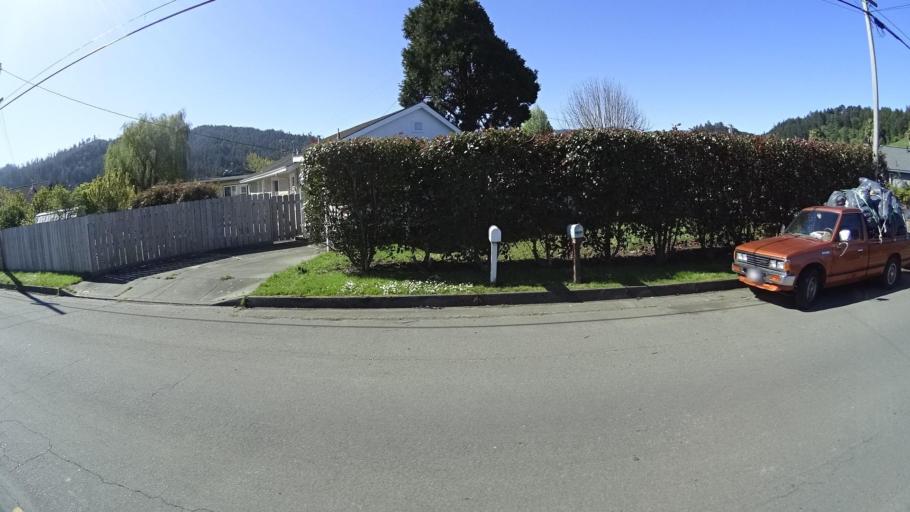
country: US
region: California
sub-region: Humboldt County
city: Rio Dell
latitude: 40.4991
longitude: -124.1030
